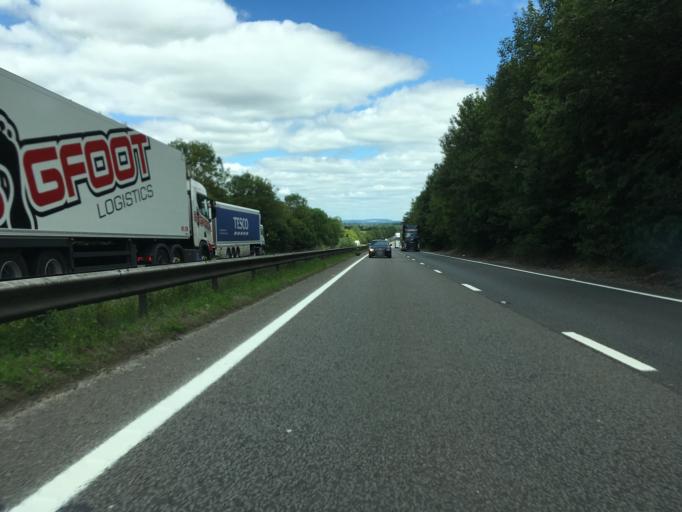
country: GB
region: England
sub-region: Hampshire
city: Kings Worthy
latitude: 51.1209
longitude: -1.3449
